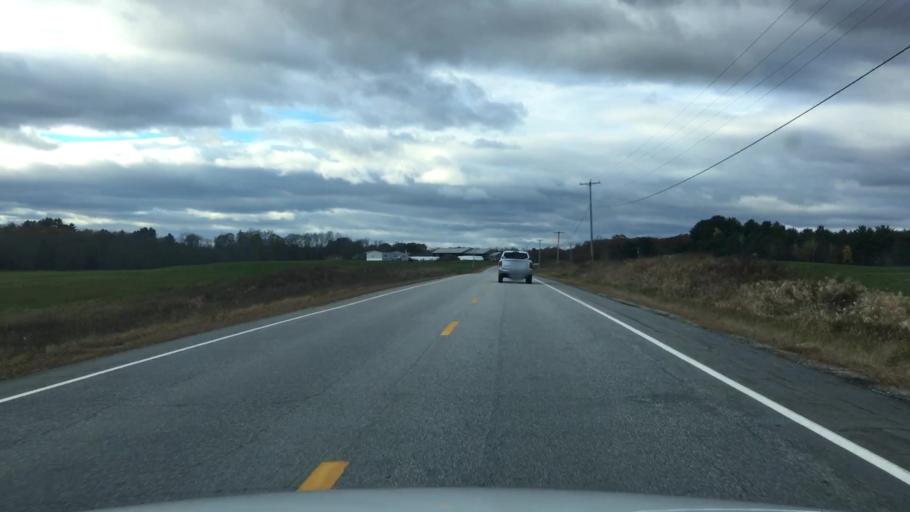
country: US
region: Maine
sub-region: Androscoggin County
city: Leeds
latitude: 44.3344
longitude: -70.1285
